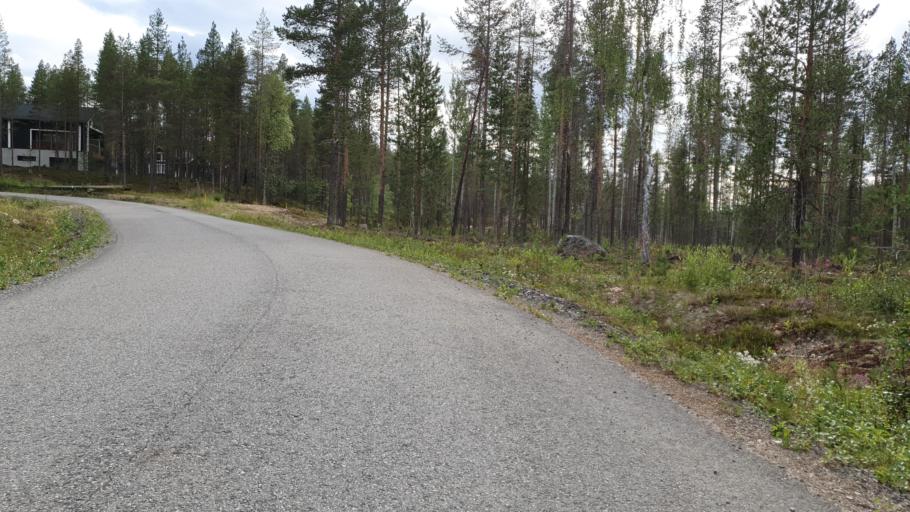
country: FI
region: Lapland
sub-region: Tunturi-Lappi
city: Kolari
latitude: 67.5934
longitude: 24.1300
